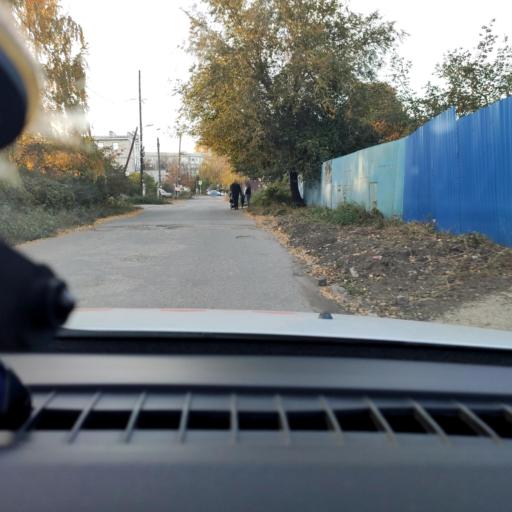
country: RU
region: Samara
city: Samara
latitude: 53.1886
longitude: 50.2113
